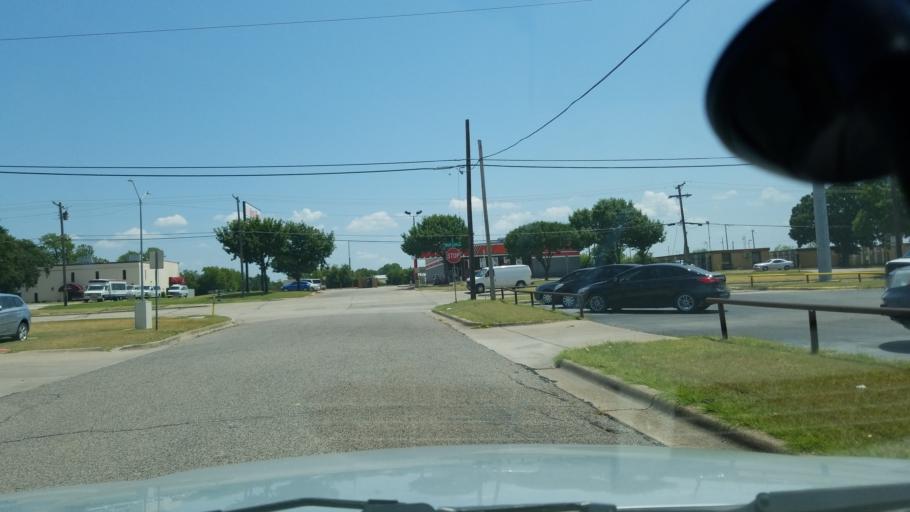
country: US
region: Texas
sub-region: Dallas County
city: Irving
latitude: 32.8203
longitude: -96.9944
